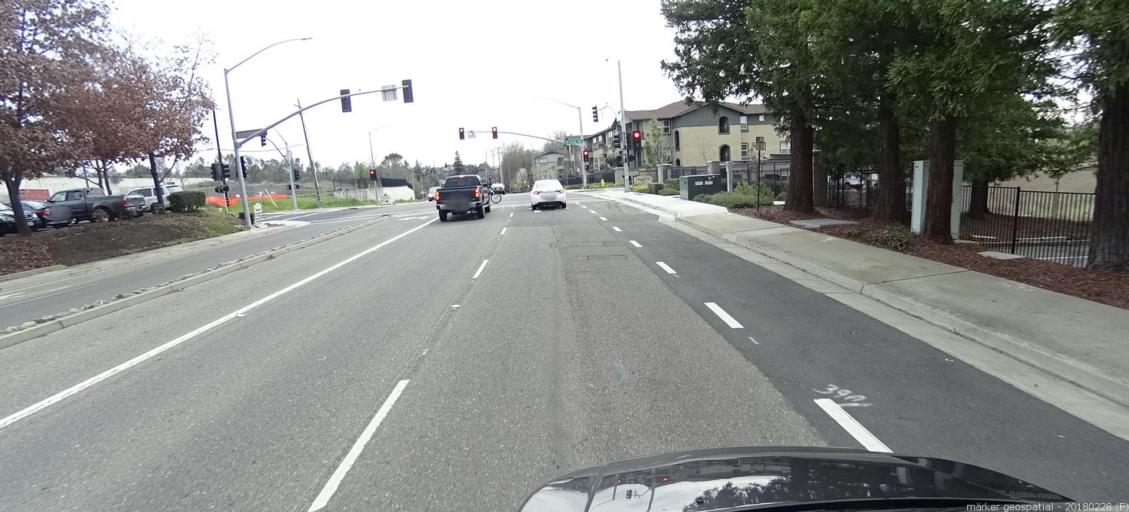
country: US
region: California
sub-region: Sacramento County
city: Folsom
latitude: 38.6598
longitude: -121.1698
